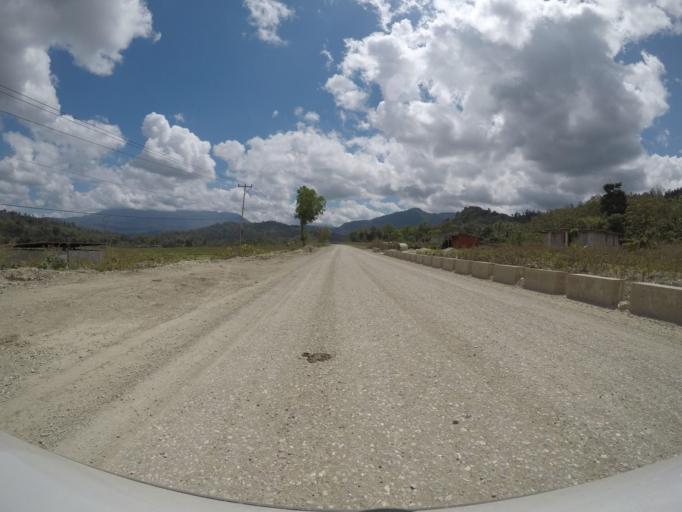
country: TL
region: Viqueque
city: Viqueque
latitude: -8.8273
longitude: 126.3770
